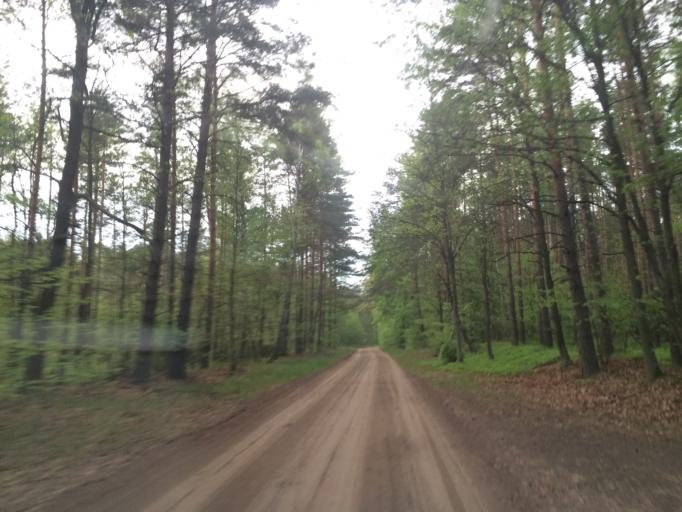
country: PL
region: Warmian-Masurian Voivodeship
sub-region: Powiat nowomiejski
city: Kurzetnik
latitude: 53.3586
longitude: 19.5183
